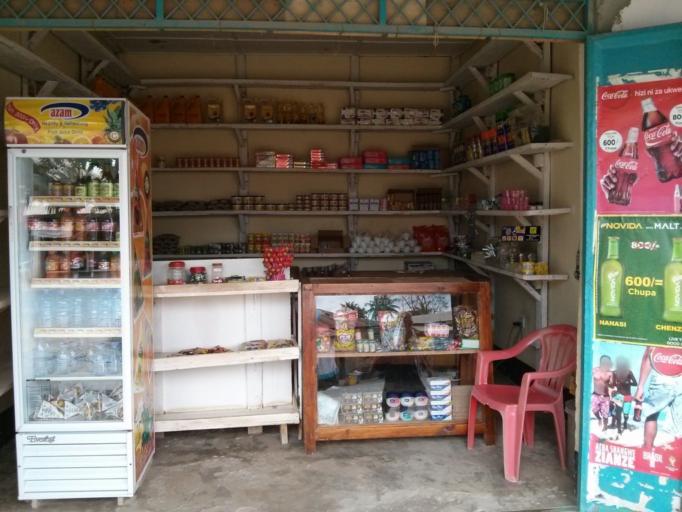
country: TZ
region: Pwani
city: Bagamoyo
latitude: -6.4400
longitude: 38.9057
